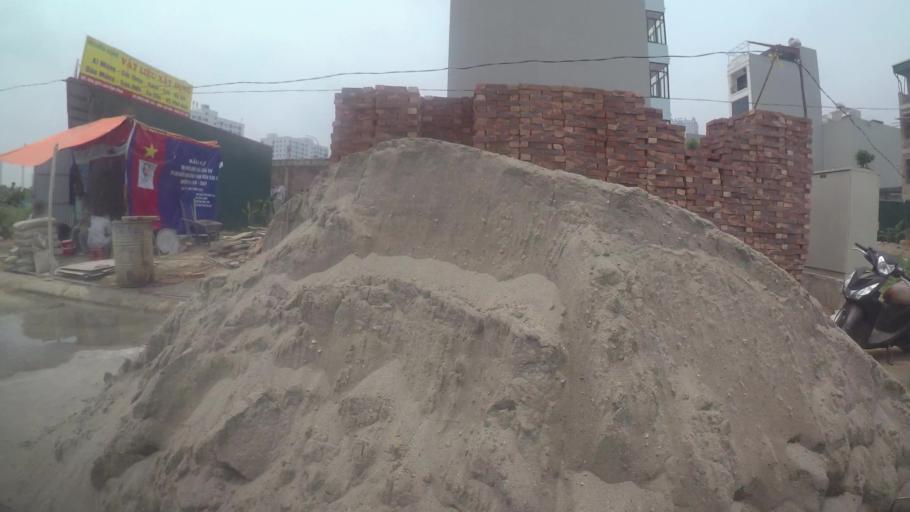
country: VN
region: Ha Noi
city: Ha Dong
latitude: 20.9773
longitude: 105.7696
